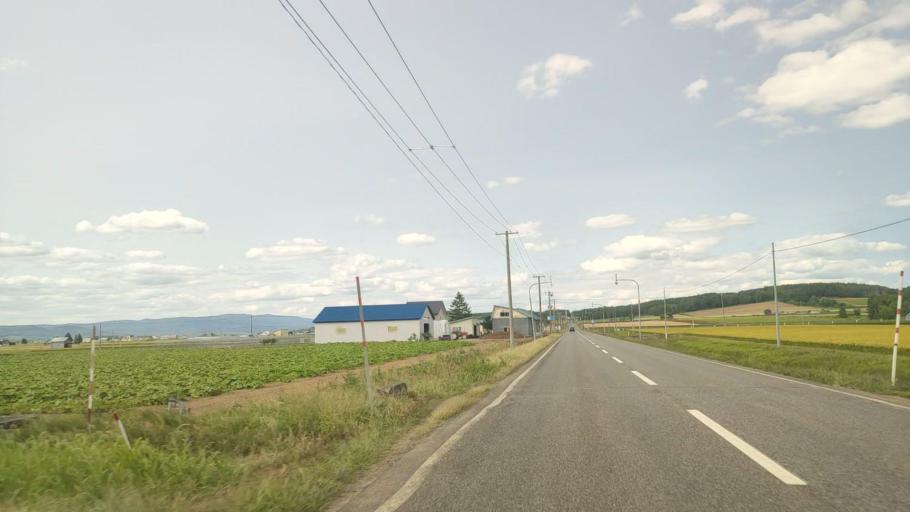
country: JP
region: Hokkaido
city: Nayoro
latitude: 44.2293
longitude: 142.4157
